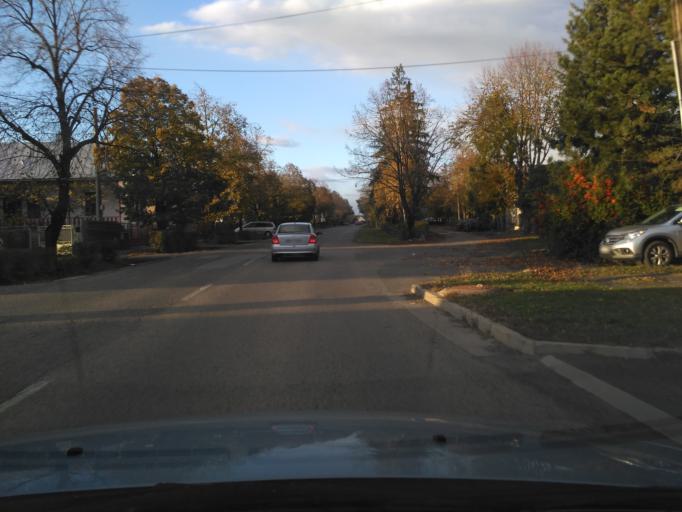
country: SK
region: Kosicky
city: Trebisov
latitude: 48.6464
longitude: 21.6798
